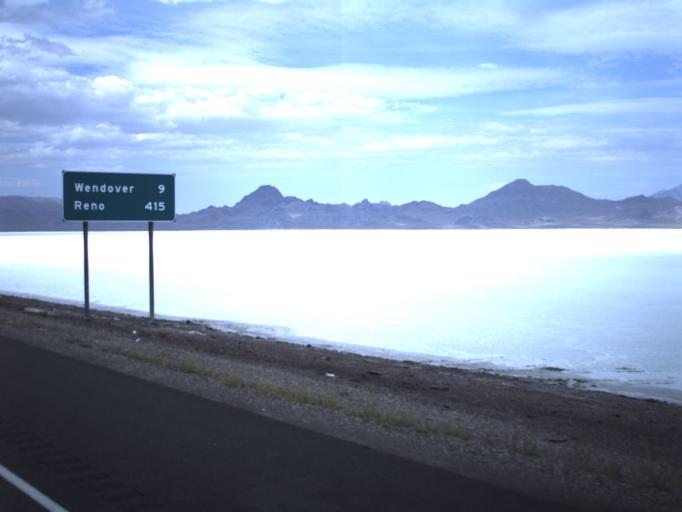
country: US
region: Utah
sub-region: Tooele County
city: Wendover
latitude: 40.7398
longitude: -113.8693
